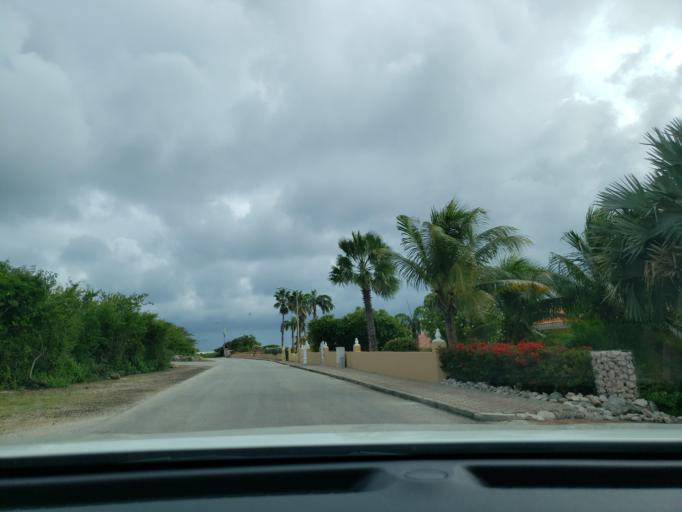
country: CW
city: Dorp Soto
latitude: 12.1980
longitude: -69.0763
